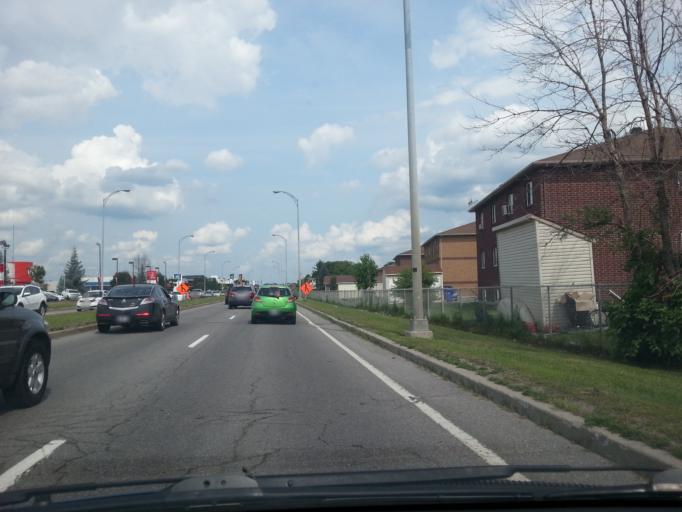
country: CA
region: Quebec
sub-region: Outaouais
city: Gatineau
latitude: 45.4883
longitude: -75.7089
